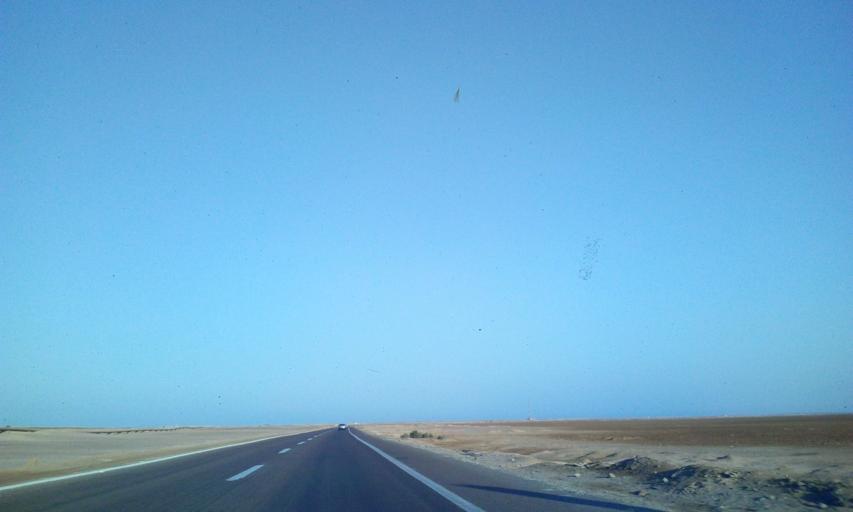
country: EG
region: South Sinai
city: Tor
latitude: 28.2729
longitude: 33.1374
